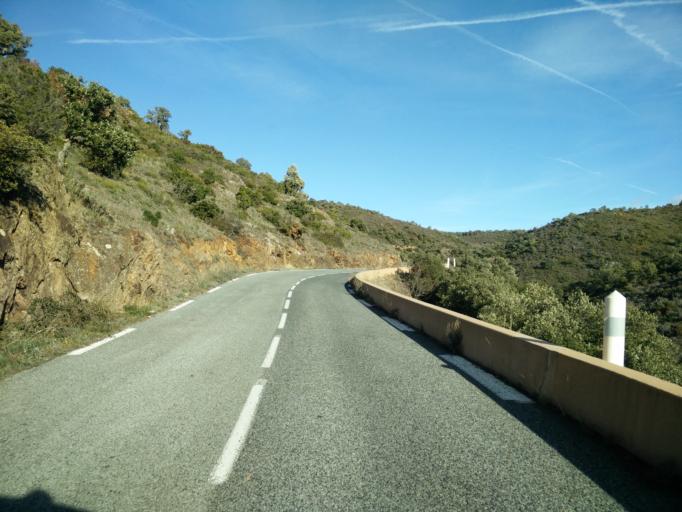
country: FR
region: Provence-Alpes-Cote d'Azur
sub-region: Departement du Var
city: Saint-Raphael
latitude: 43.4955
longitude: 6.7802
